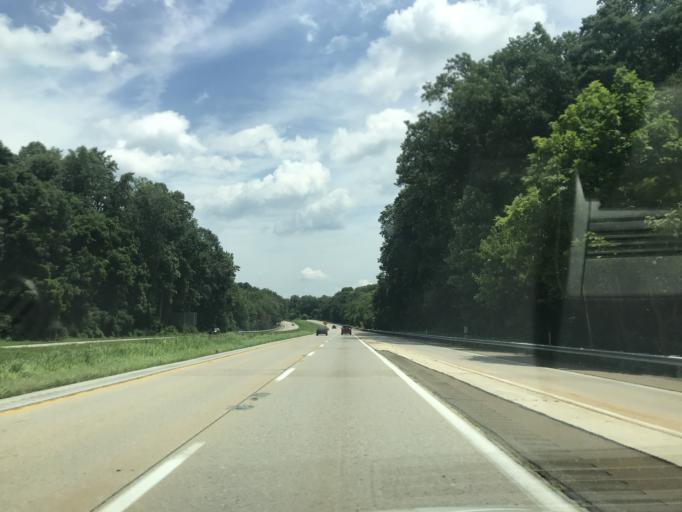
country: US
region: Pennsylvania
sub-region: Chester County
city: Kennett Square
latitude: 39.8564
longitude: -75.7120
